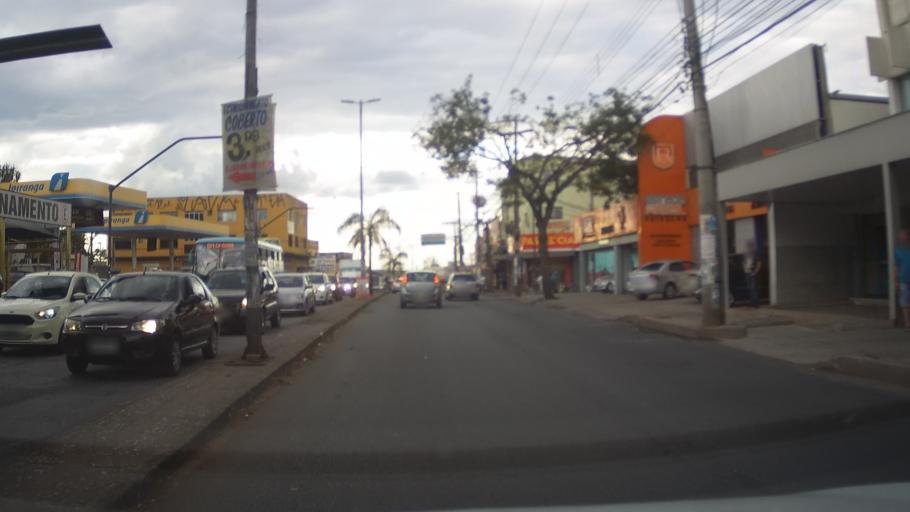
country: BR
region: Minas Gerais
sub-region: Contagem
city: Contagem
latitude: -19.9656
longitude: -44.0153
